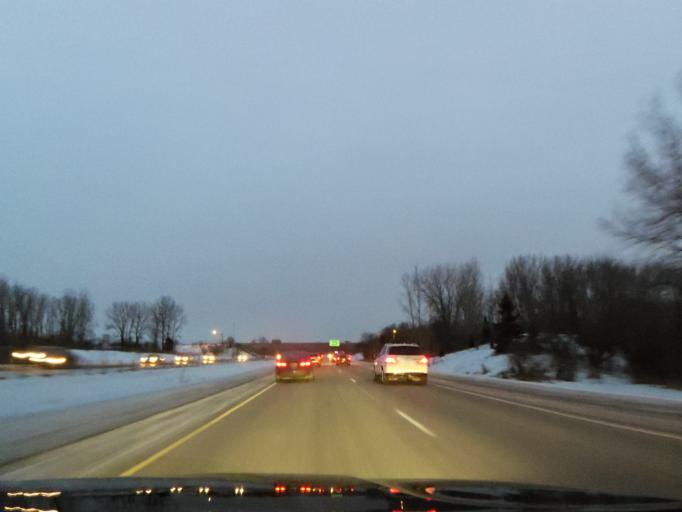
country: US
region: Minnesota
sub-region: Ramsey County
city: North Saint Paul
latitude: 45.0089
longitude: -92.9582
